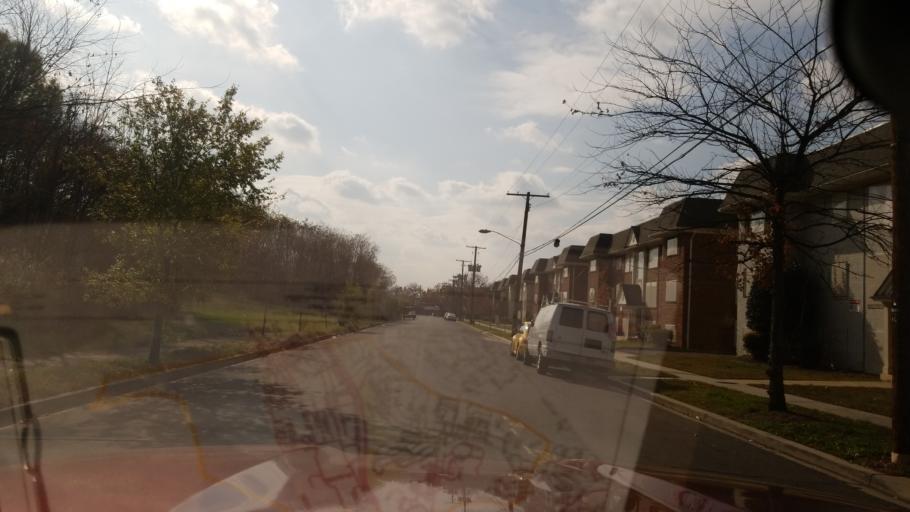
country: US
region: Maryland
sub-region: Prince George's County
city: Glassmanor
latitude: 38.8281
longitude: -76.9958
